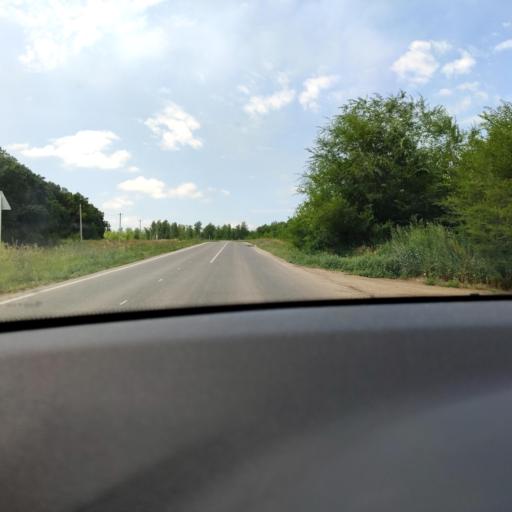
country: RU
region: Samara
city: Petra-Dubrava
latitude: 53.3483
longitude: 50.4996
